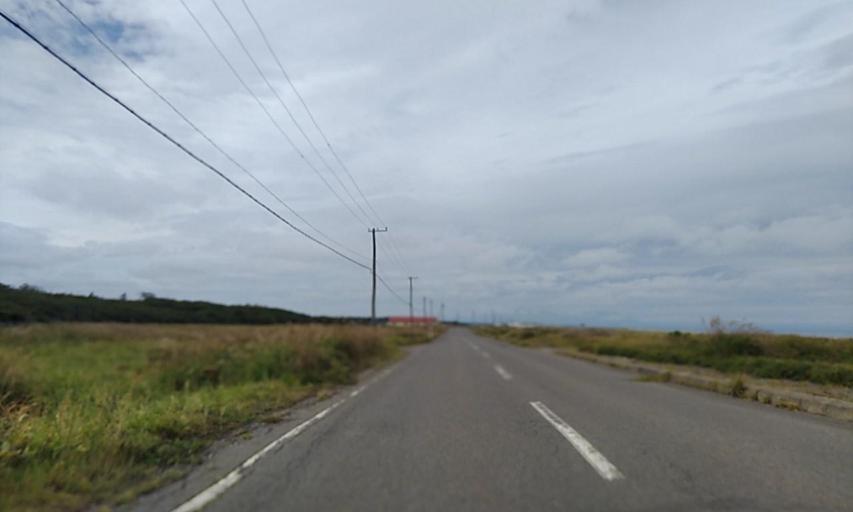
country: JP
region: Hokkaido
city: Shibetsu
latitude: 43.6076
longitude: 145.2829
